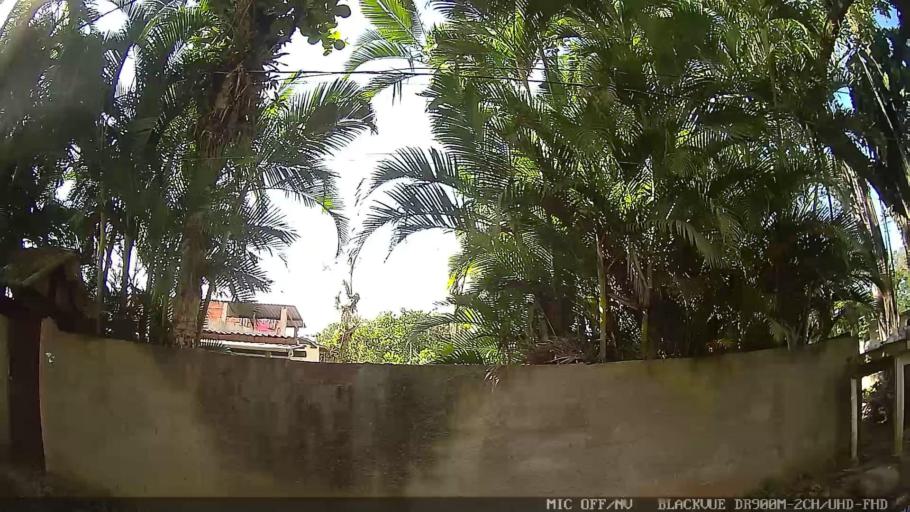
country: BR
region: Sao Paulo
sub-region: Peruibe
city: Peruibe
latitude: -24.2697
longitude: -46.9313
